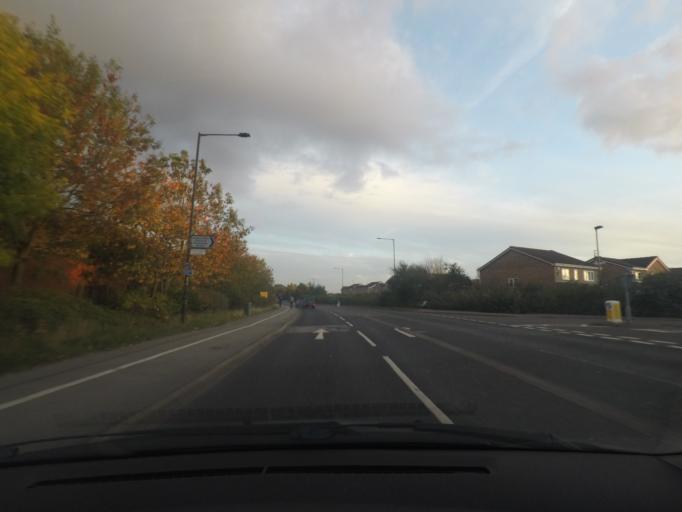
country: GB
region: England
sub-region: City of York
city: Skelton
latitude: 53.9876
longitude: -1.1038
